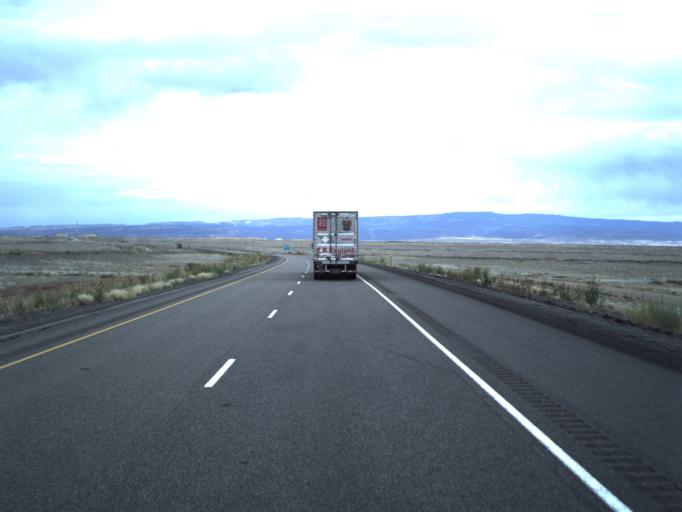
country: US
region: Utah
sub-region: Grand County
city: Moab
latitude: 38.9321
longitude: -109.4360
